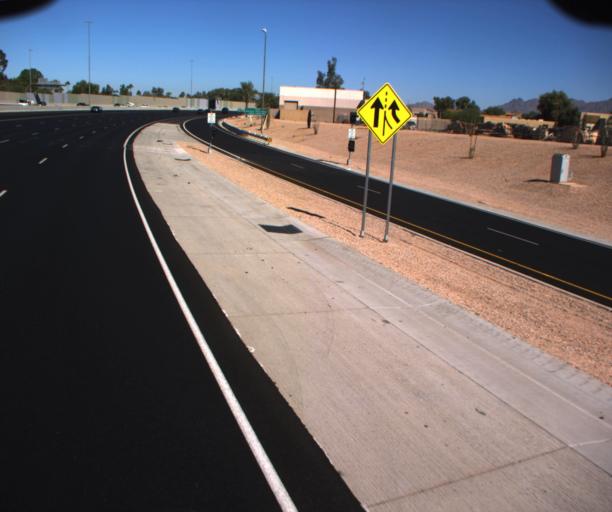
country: US
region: Arizona
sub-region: Maricopa County
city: Scottsdale
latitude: 33.5668
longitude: -111.8905
